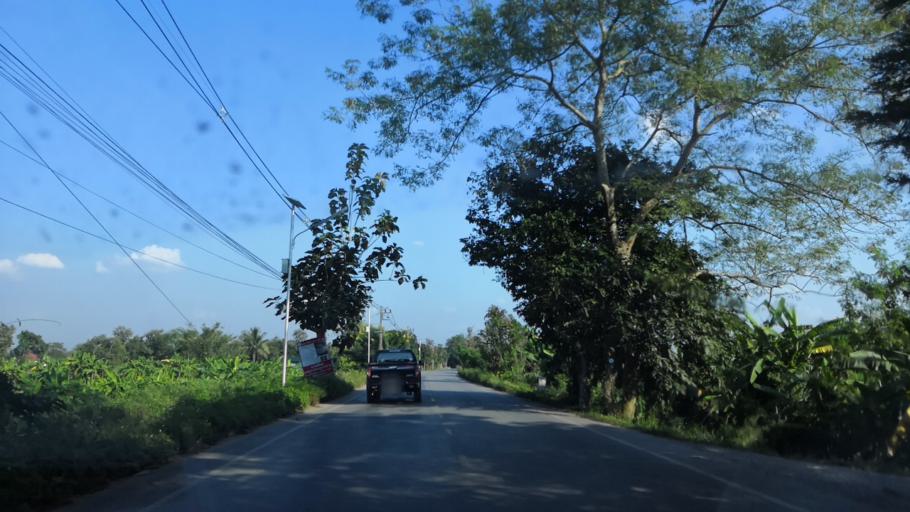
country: TH
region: Chiang Rai
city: Chiang Rai
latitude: 19.9331
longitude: 99.8909
